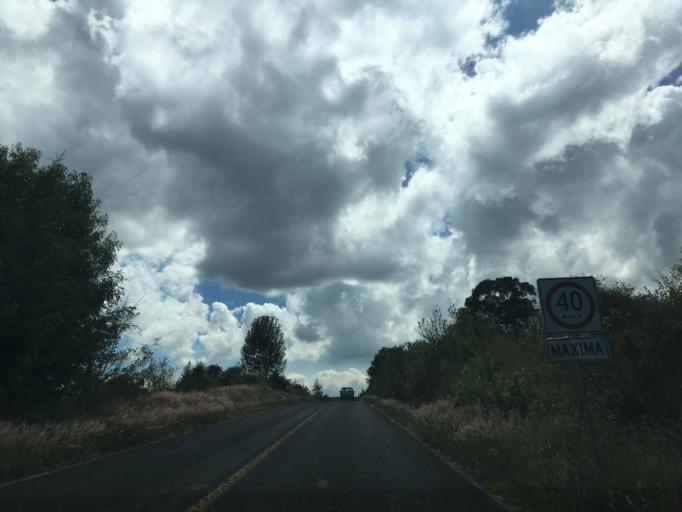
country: MX
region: Michoacan
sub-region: Morelia
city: Cuto de la Esperanza
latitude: 19.7760
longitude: -101.3981
